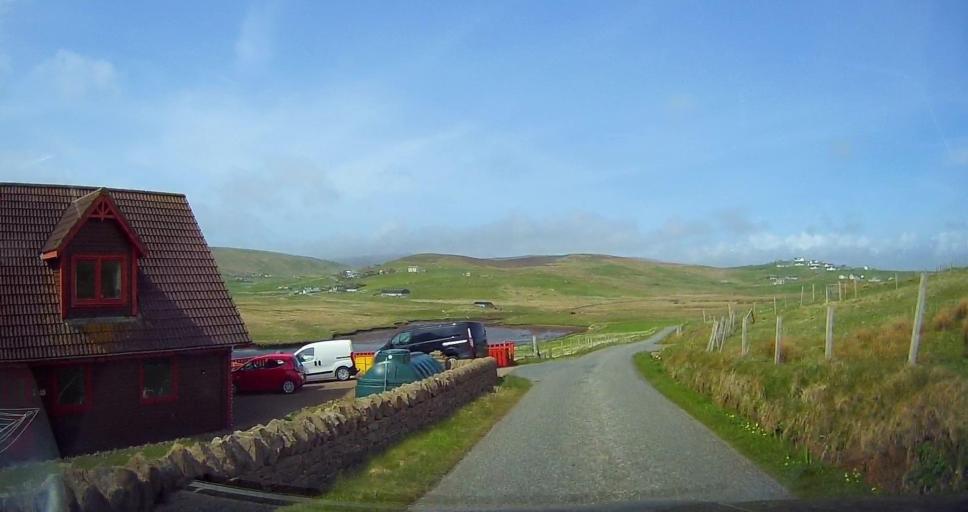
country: GB
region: Scotland
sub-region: Shetland Islands
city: Sandwick
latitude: 60.0441
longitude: -1.2055
